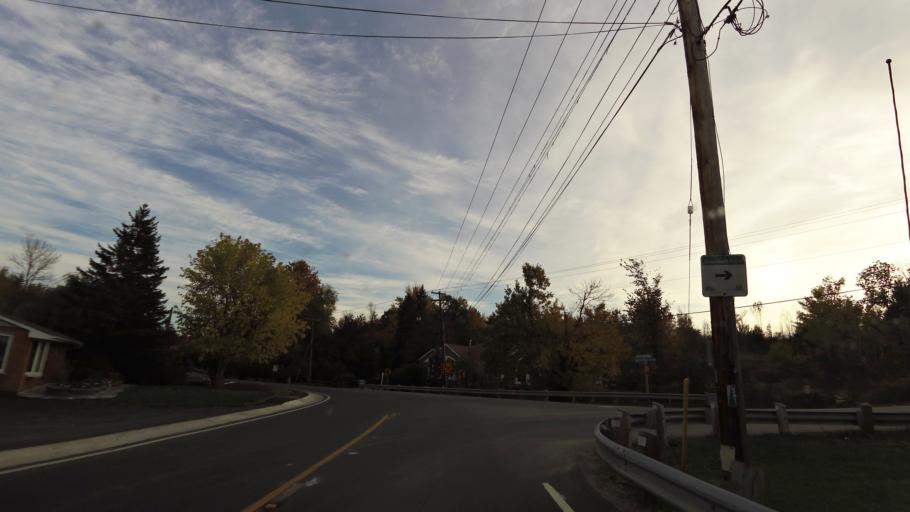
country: CA
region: Ontario
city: Brampton
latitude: 43.7114
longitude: -79.9375
